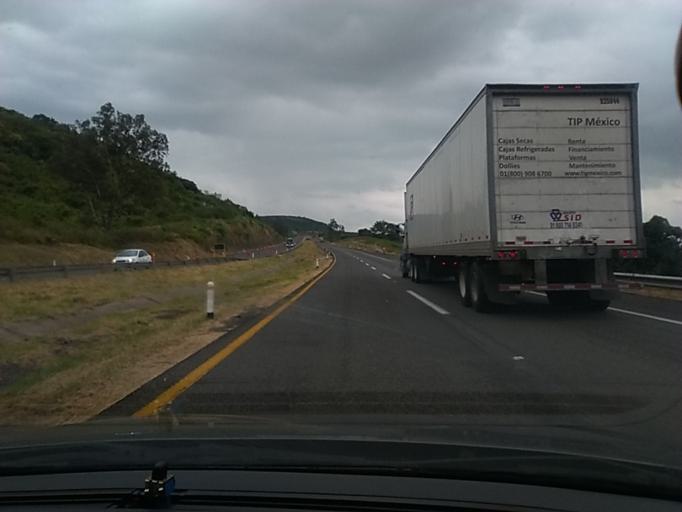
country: MX
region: Jalisco
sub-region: Zapotlan del Rey
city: Zapotlan del Rey
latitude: 20.4877
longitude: -102.9420
